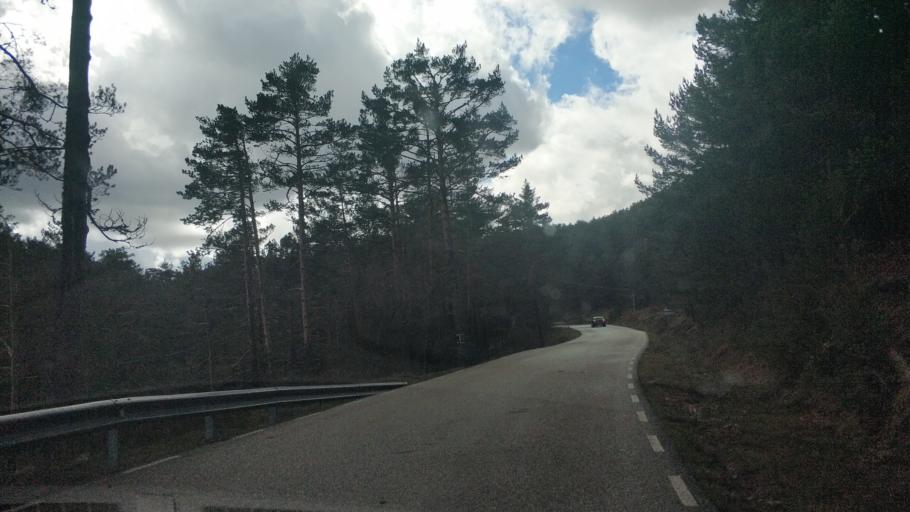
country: ES
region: Castille and Leon
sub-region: Provincia de Burgos
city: Neila
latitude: 42.0256
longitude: -3.0120
